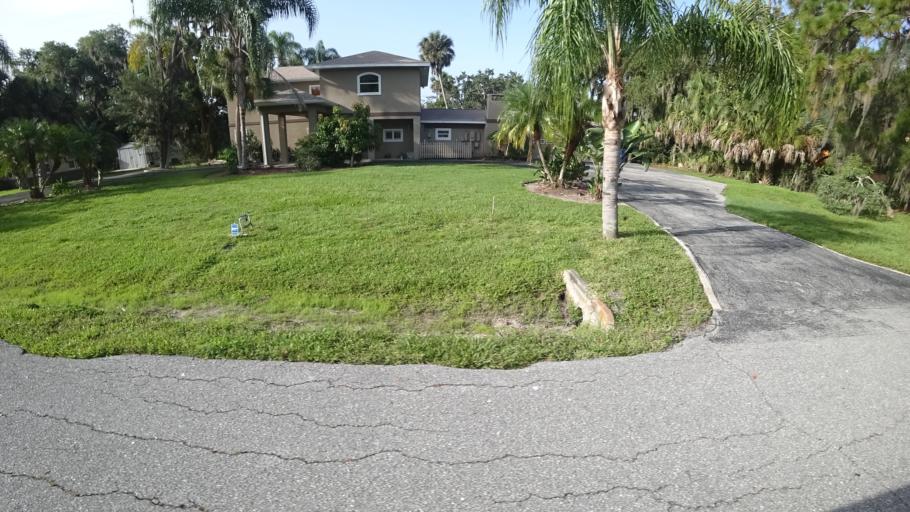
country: US
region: Florida
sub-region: Sarasota County
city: Desoto Lakes
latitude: 27.4199
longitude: -82.4713
